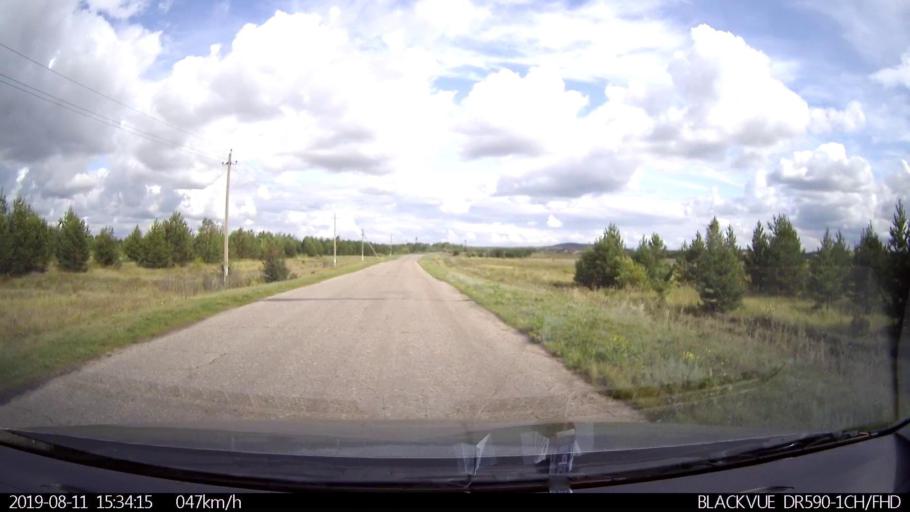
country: RU
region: Ulyanovsk
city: Ignatovka
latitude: 53.8618
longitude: 47.5932
